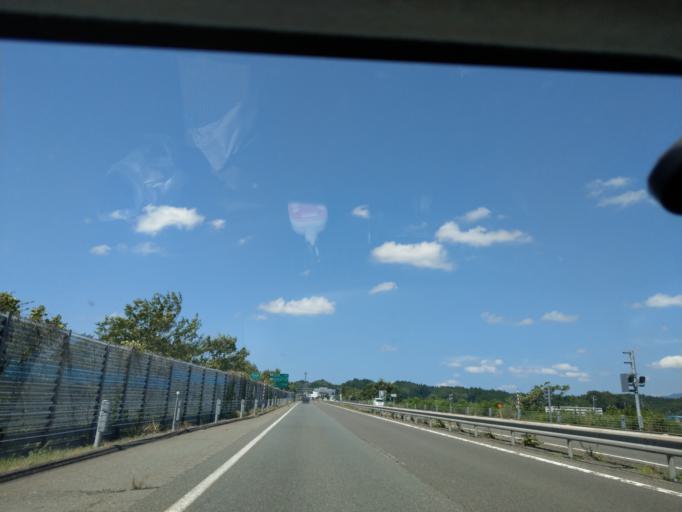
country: JP
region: Akita
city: Akita
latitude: 39.6460
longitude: 140.2083
